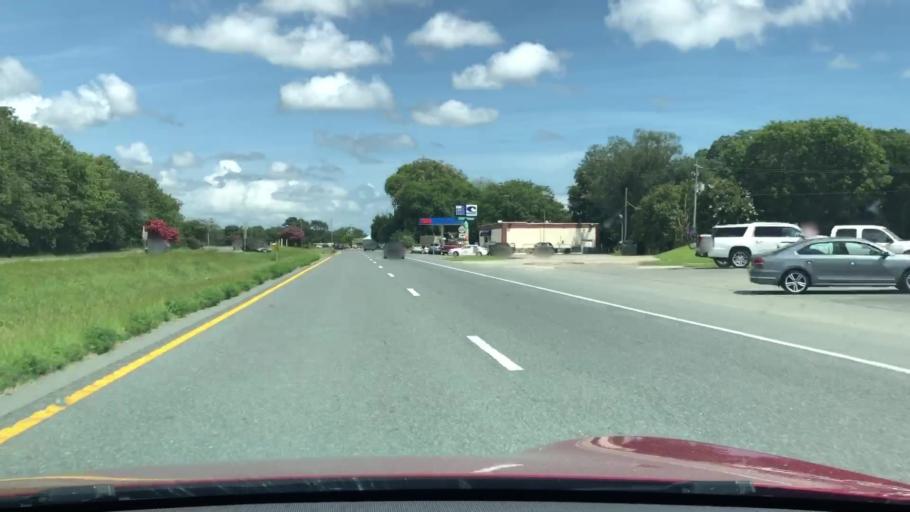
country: US
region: Virginia
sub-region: Northampton County
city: Eastville
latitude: 37.4030
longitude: -75.9051
